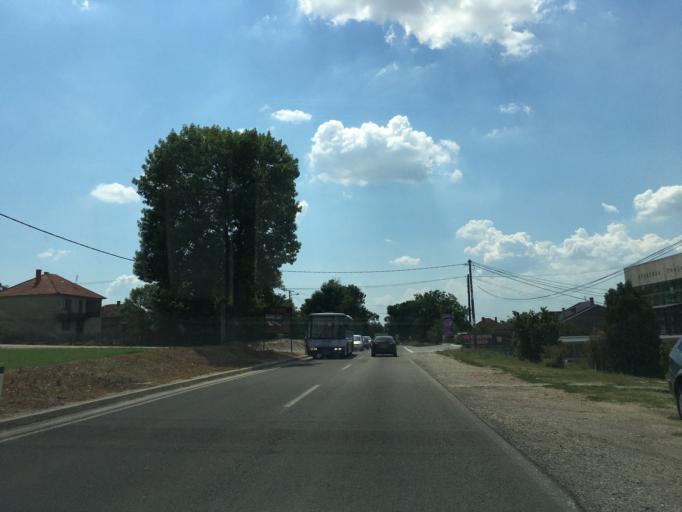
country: RS
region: Central Serbia
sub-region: Belgrade
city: Mladenovac
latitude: 44.4667
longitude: 20.6672
